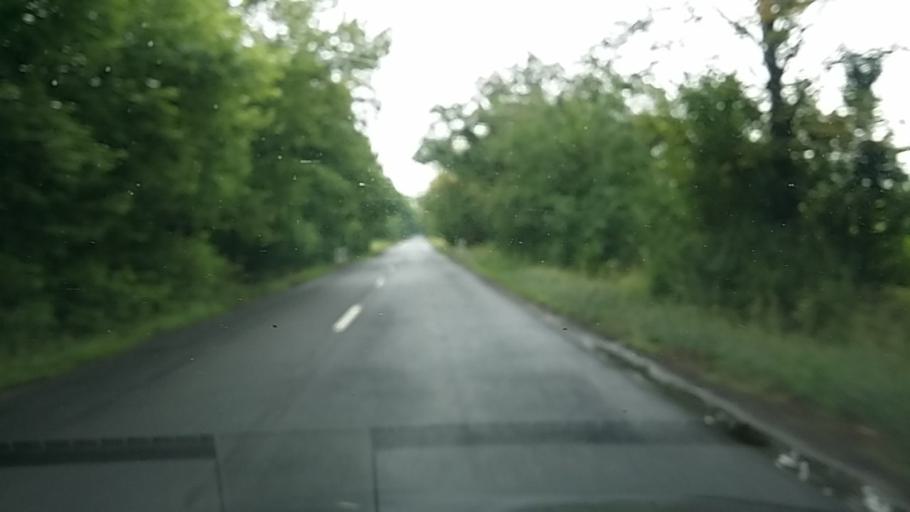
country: HU
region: Pest
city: Szob
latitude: 47.9512
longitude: 18.7813
